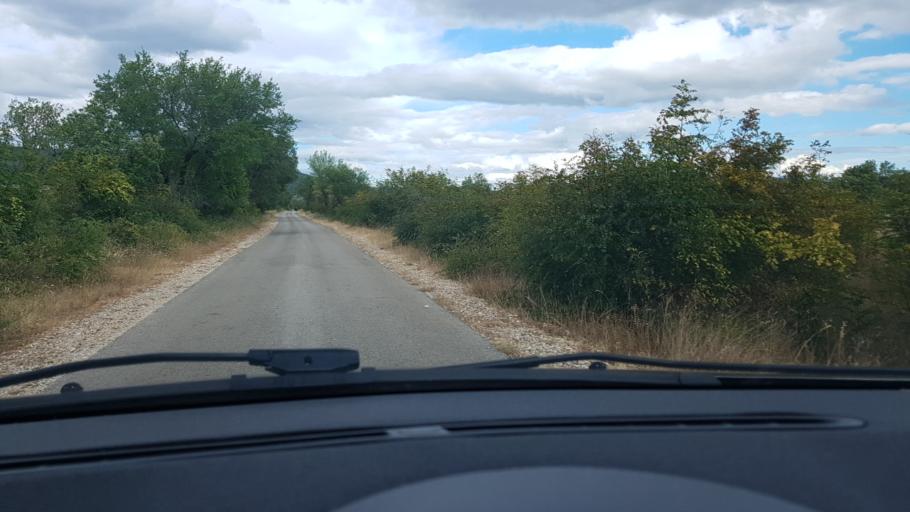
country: HR
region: Sibensko-Kniniska
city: Kistanje
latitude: 44.1078
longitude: 15.9322
